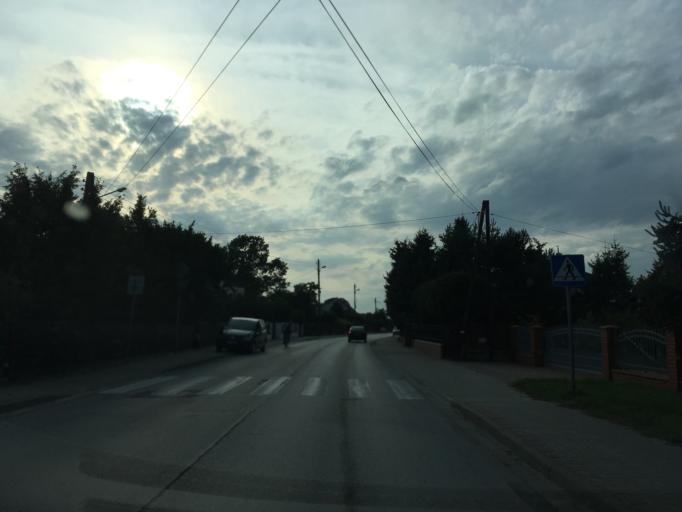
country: PL
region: Swietokrzyskie
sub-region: Powiat wloszczowski
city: Wloszczowa
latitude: 50.8480
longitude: 19.9915
